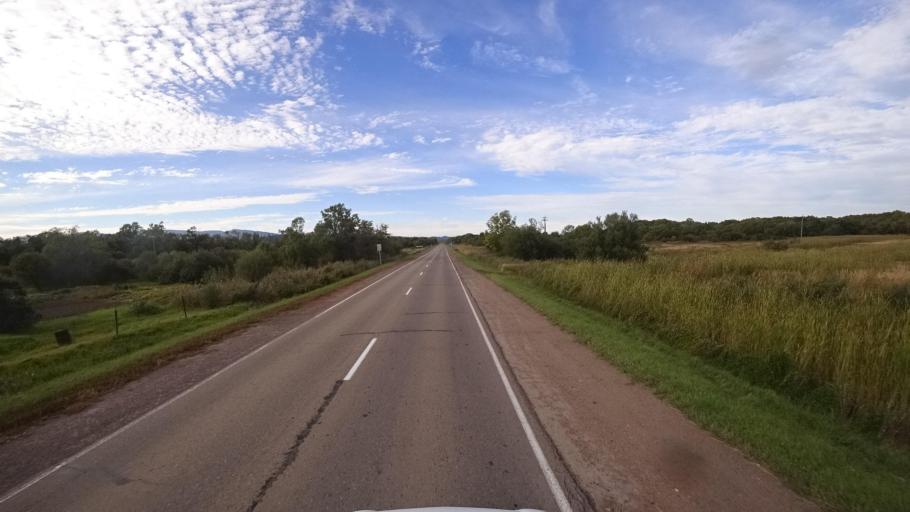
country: RU
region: Primorskiy
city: Dostoyevka
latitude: 44.2995
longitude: 133.4261
